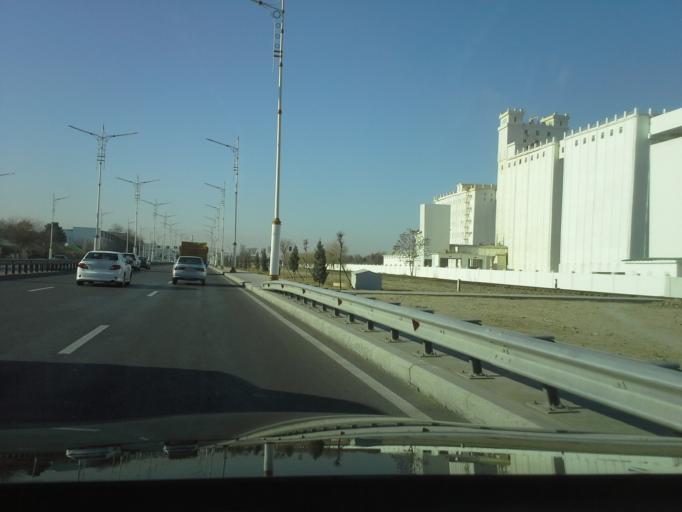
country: TM
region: Ahal
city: Ashgabat
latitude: 37.9548
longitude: 58.3742
